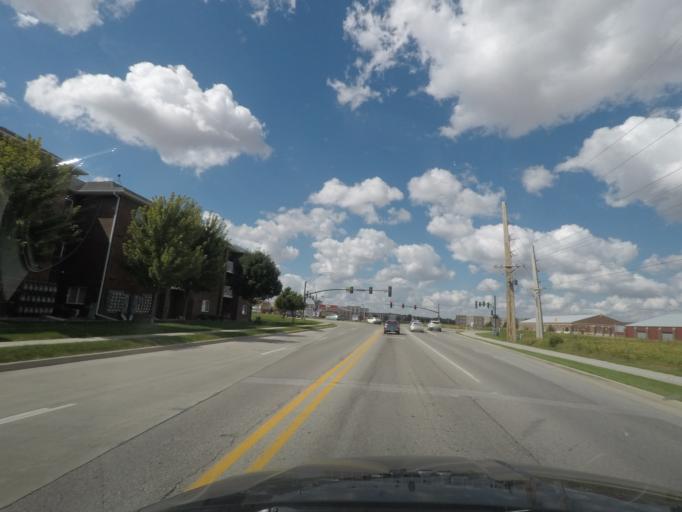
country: US
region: Iowa
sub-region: Story County
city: Ames
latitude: 42.0121
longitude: -93.6776
